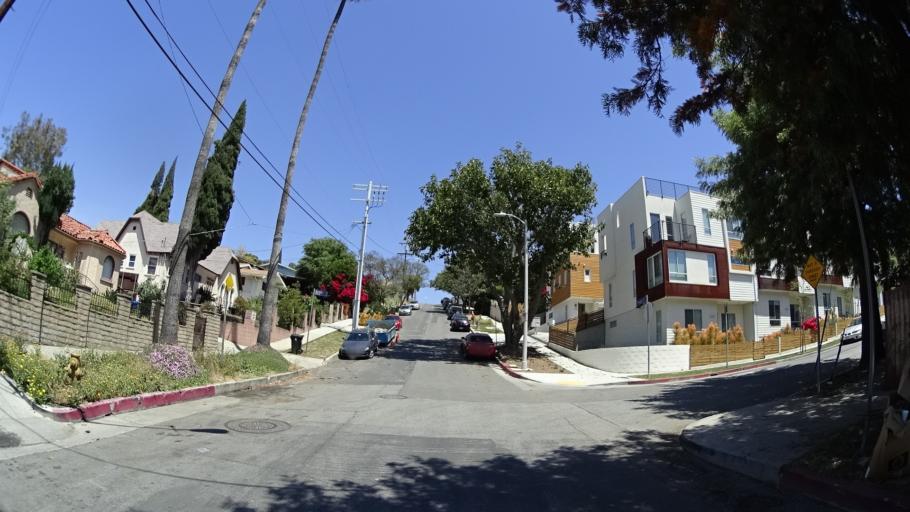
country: US
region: California
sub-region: Los Angeles County
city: Echo Park
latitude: 34.0751
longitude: -118.2511
